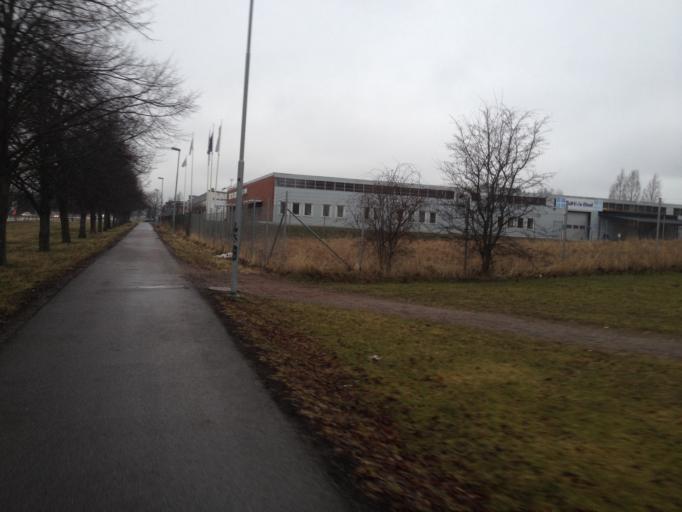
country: SE
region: OEstergoetland
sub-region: Norrkopings Kommun
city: Norrkoping
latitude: 58.6054
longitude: 16.1804
